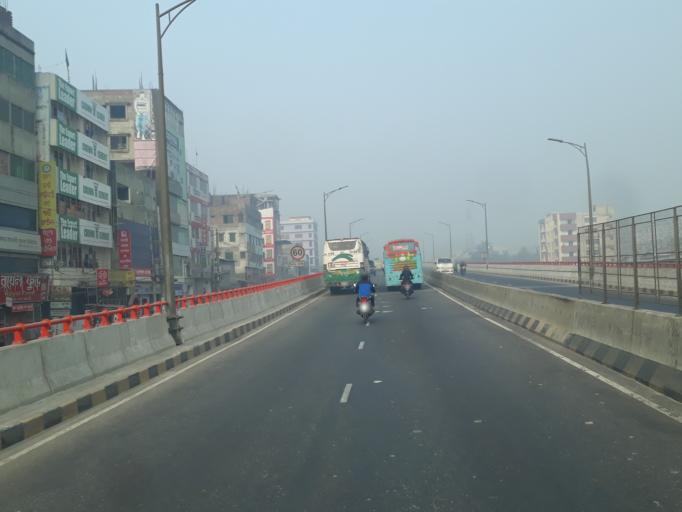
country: BD
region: Dhaka
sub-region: Dhaka
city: Dhaka
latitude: 23.7079
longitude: 90.4392
